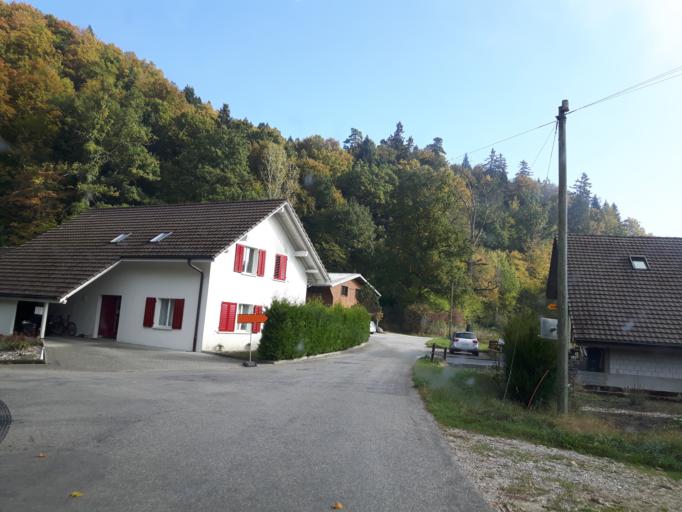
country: CH
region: Bern
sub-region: Oberaargau
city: Roggwil
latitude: 47.2418
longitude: 7.8306
